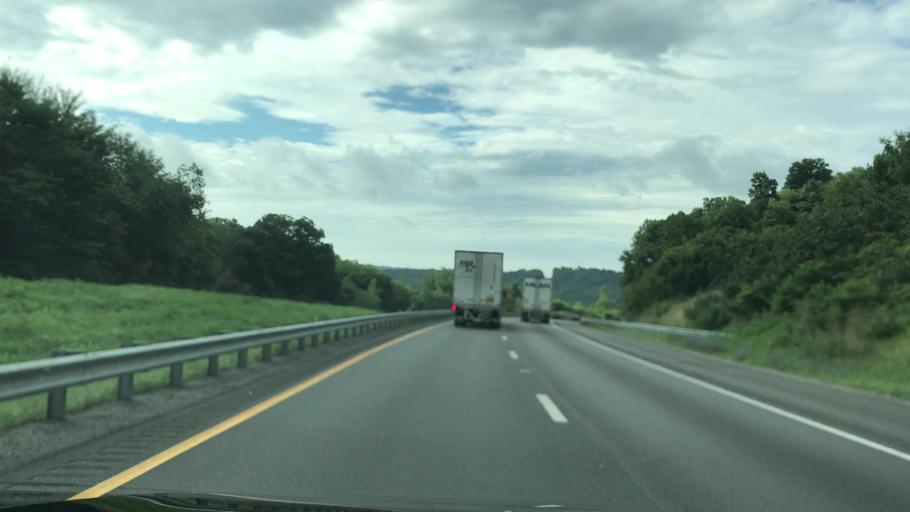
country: US
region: Virginia
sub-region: Pulaski County
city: Pulaski
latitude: 36.9018
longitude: -80.8765
